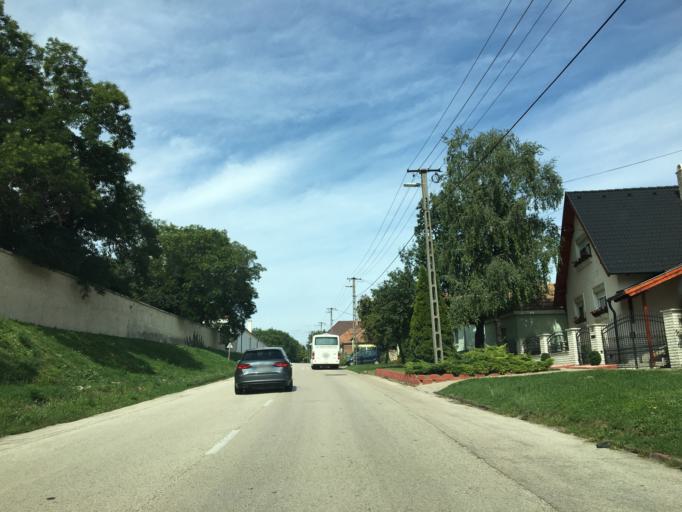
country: HU
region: Komarom-Esztergom
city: Bajna
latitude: 47.6523
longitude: 18.6047
